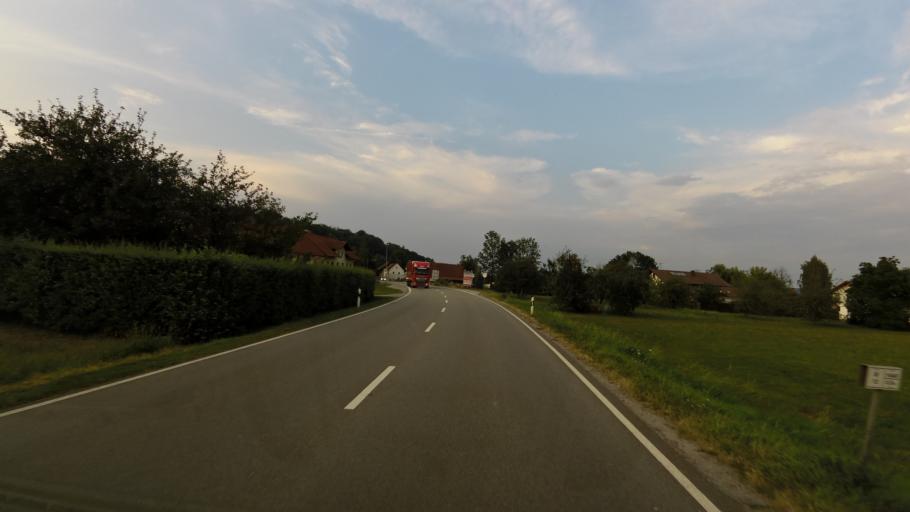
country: DE
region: Bavaria
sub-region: Lower Bavaria
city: Kirchham
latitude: 48.3485
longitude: 13.2481
